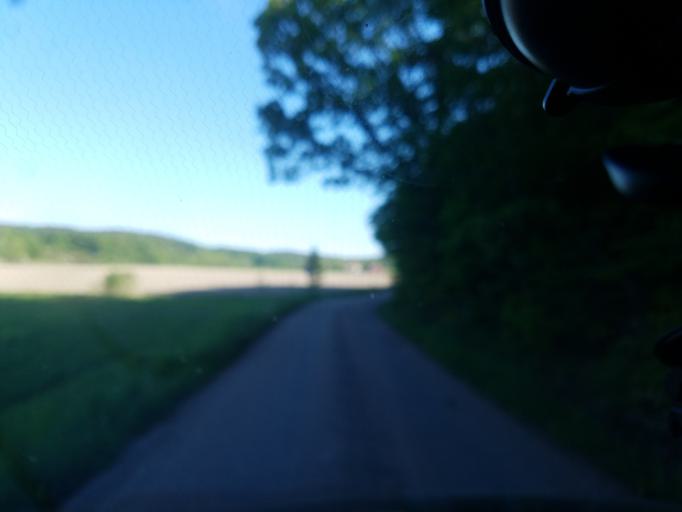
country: SE
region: Vaestra Goetaland
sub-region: Orust
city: Henan
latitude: 58.2850
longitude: 11.6405
